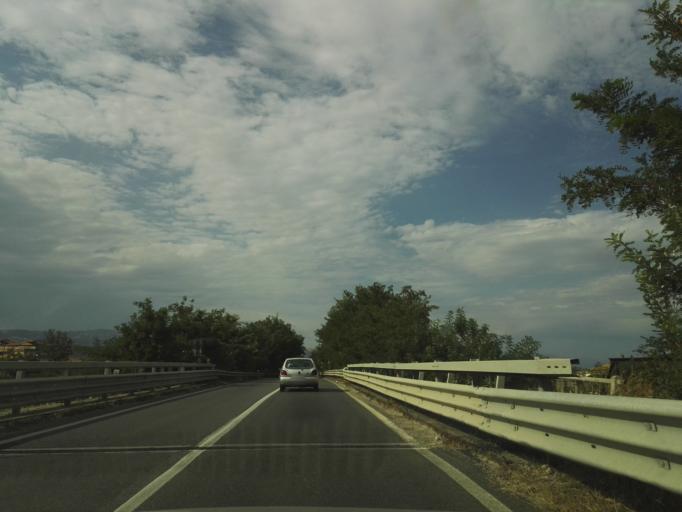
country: IT
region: Calabria
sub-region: Provincia di Catanzaro
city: Marina di Davoli
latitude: 38.6544
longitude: 16.5477
